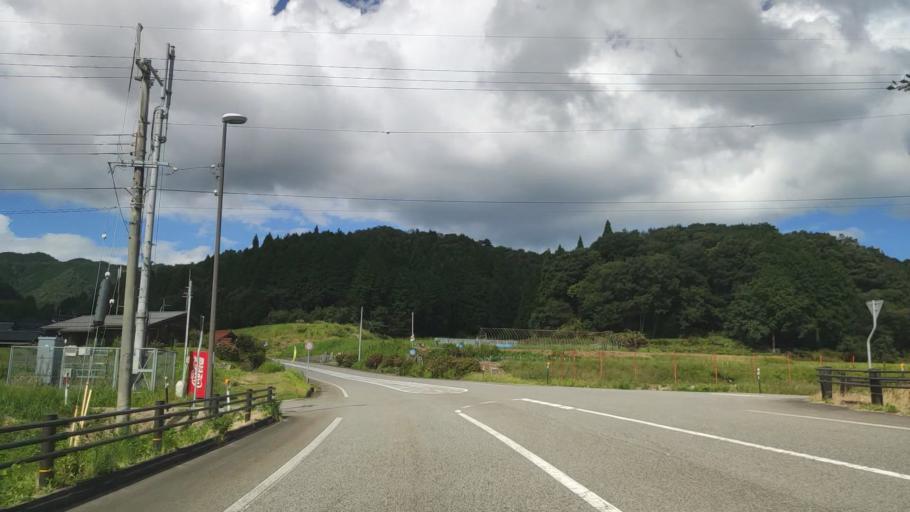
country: JP
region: Hyogo
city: Toyooka
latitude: 35.5095
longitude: 134.9923
